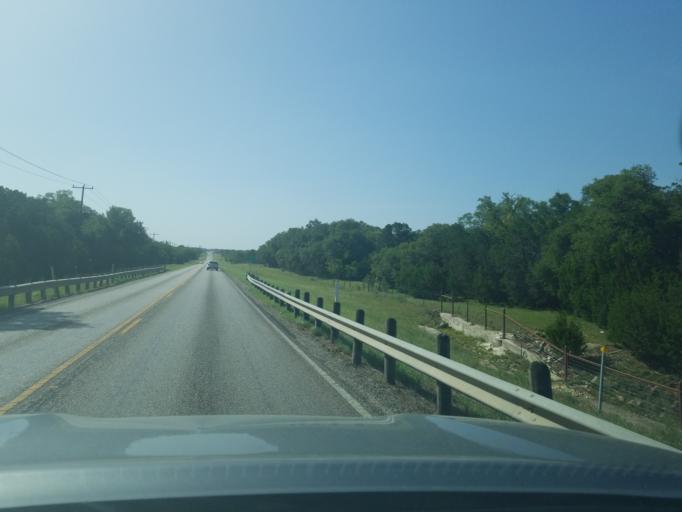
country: US
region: Texas
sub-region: Comal County
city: Garden Ridge
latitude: 29.6779
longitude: -98.3213
